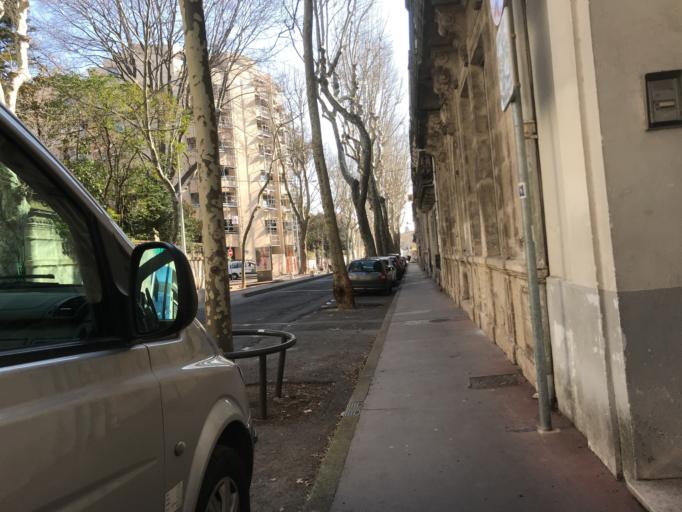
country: FR
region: Languedoc-Roussillon
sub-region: Departement de l'Herault
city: Montpellier
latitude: 43.6179
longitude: 3.8721
